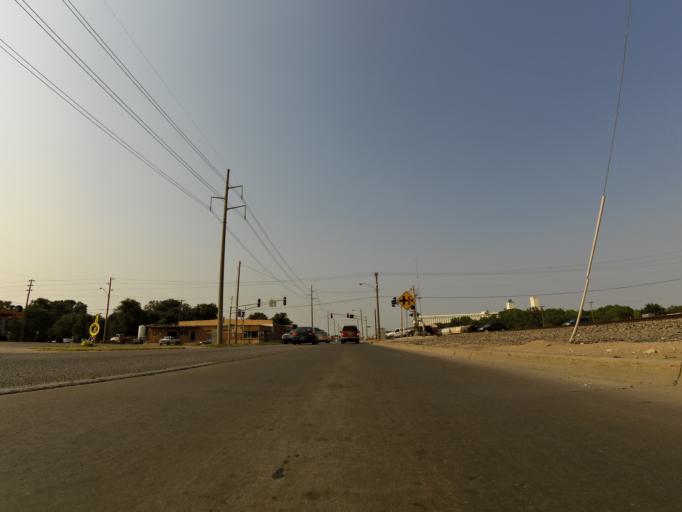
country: US
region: Kansas
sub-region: Sedgwick County
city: Wichita
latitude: 37.7369
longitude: -97.3359
